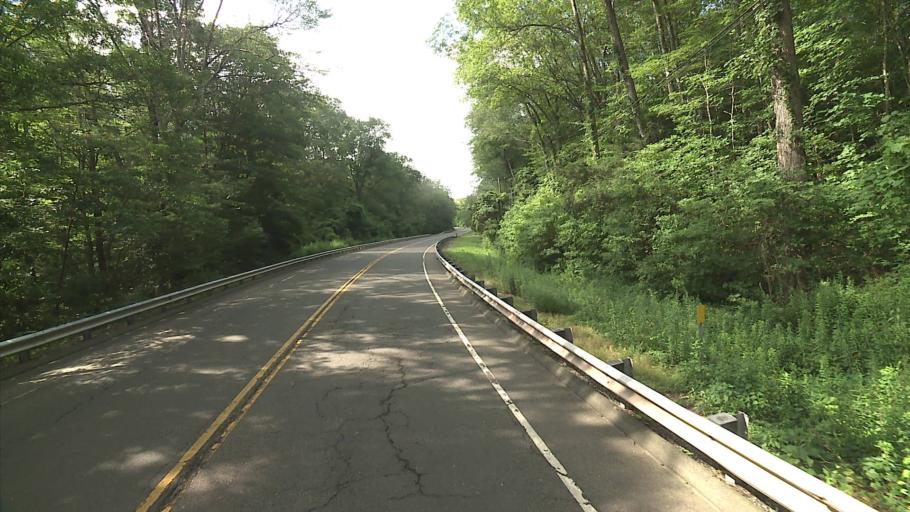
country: US
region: Connecticut
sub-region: Middlesex County
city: Deep River Center
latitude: 41.3513
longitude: -72.4965
